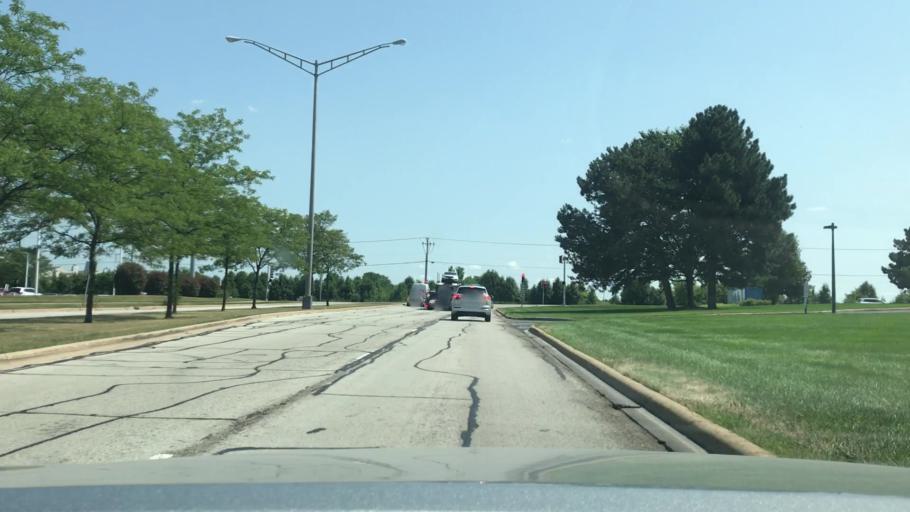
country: US
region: Illinois
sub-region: DuPage County
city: Naperville
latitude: 41.7509
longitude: -88.2180
